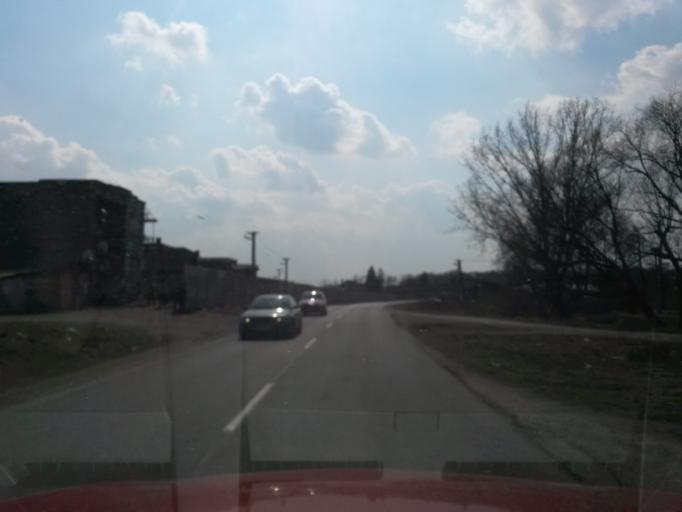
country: SK
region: Kosicky
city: Kosice
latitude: 48.6020
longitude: 21.1713
